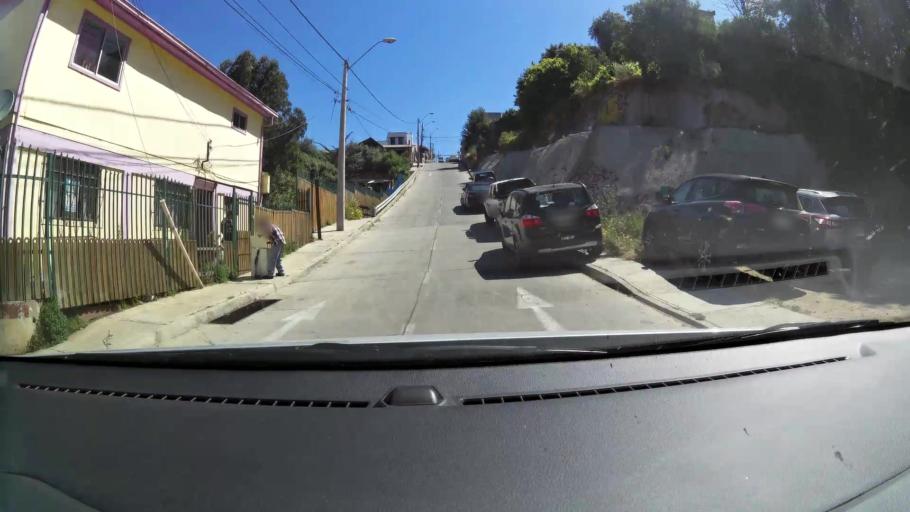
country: CL
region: Valparaiso
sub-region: Provincia de Valparaiso
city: Valparaiso
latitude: -33.0331
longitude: -71.6387
